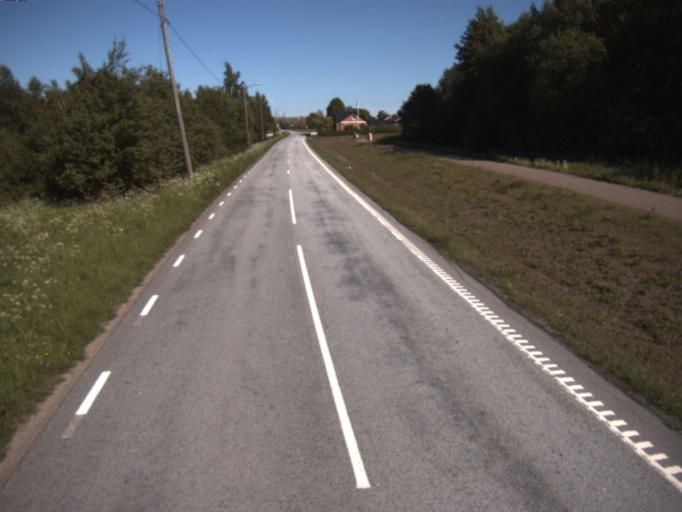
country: SE
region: Skane
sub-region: Helsingborg
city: Gantofta
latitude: 55.9928
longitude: 12.7947
